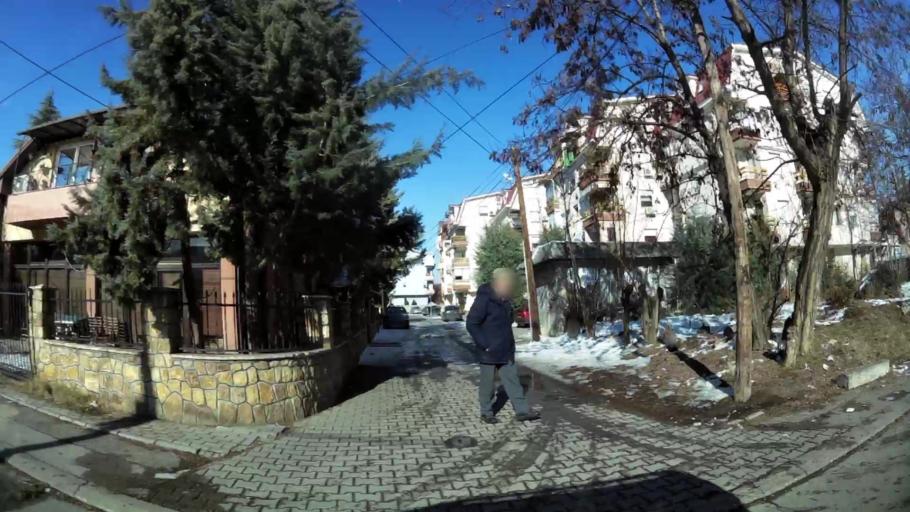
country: MK
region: Saraj
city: Saraj
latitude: 42.0076
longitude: 21.3534
